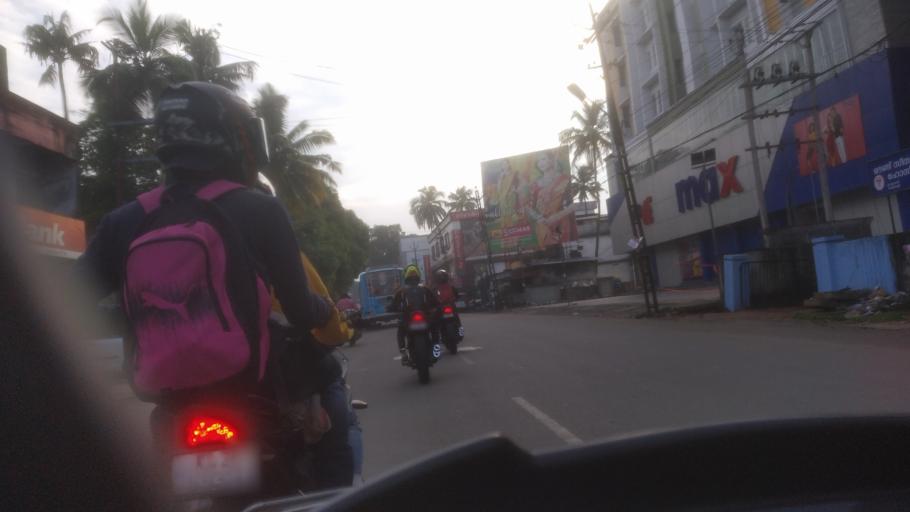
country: IN
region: Kerala
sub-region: Ernakulam
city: Perumpavur
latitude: 10.1146
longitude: 76.4699
